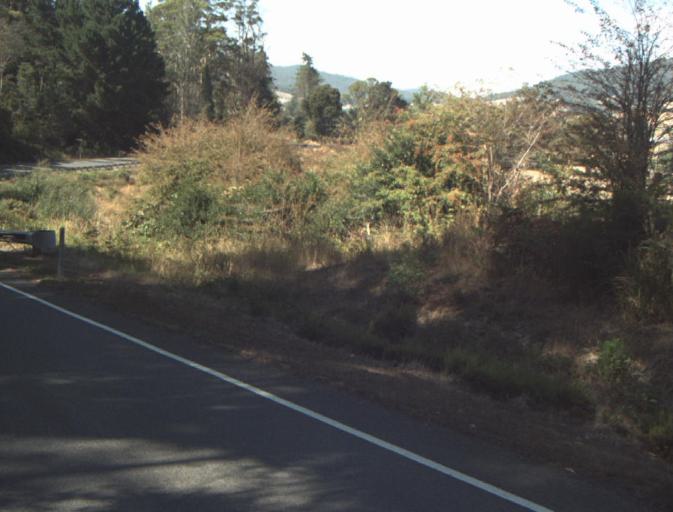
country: AU
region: Tasmania
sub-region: Launceston
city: Mayfield
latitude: -41.2271
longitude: 147.2082
